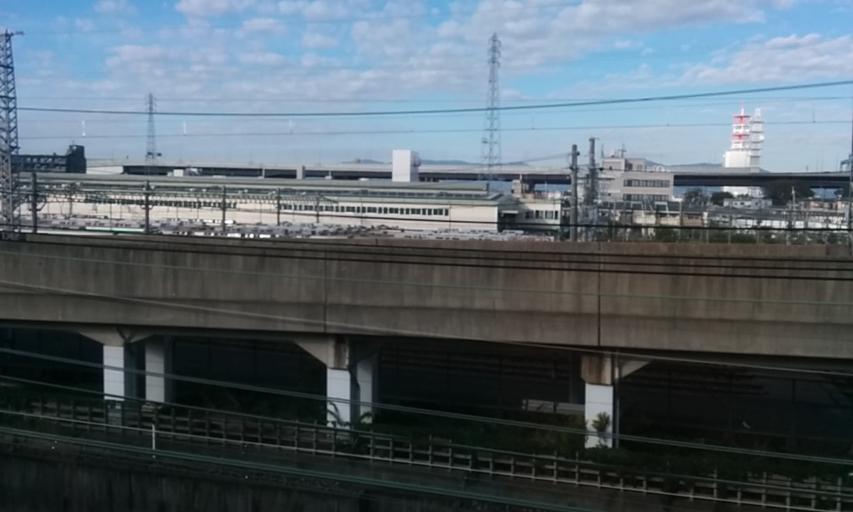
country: JP
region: Kyoto
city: Muko
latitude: 34.9590
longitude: 135.7560
